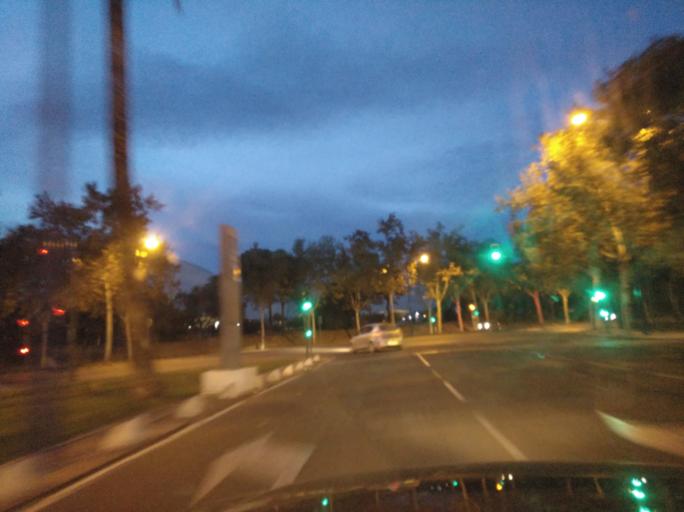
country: ES
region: Andalusia
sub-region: Provincia de Sevilla
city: Camas
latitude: 37.4071
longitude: -6.0091
